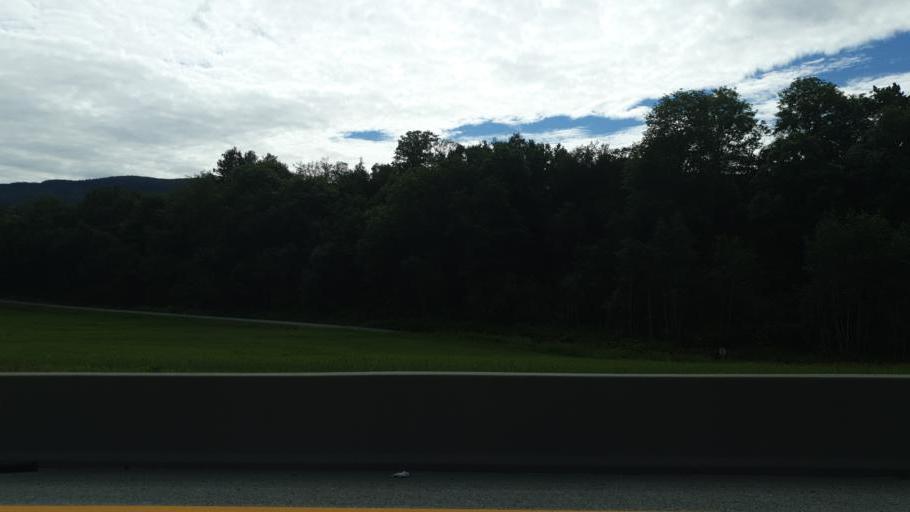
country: NO
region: Sor-Trondelag
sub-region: Melhus
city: Melhus
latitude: 63.2928
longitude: 10.2743
